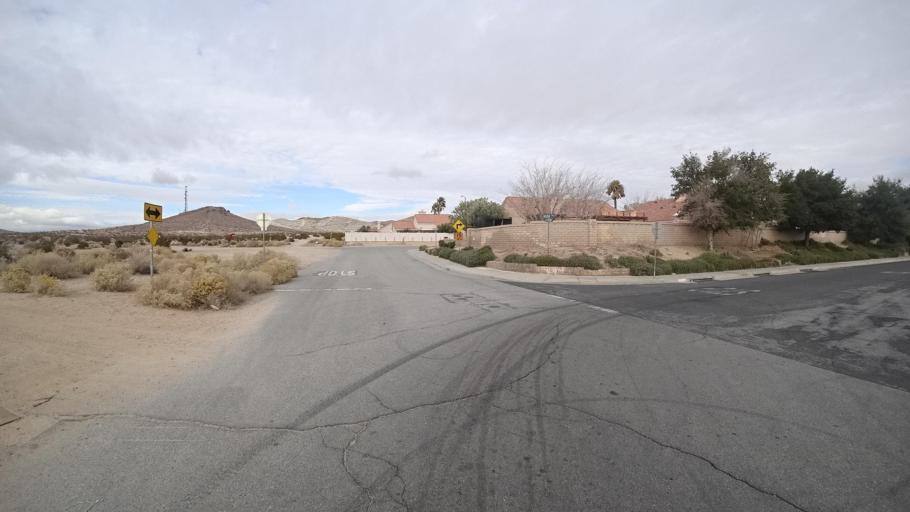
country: US
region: California
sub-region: Kern County
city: Rosamond
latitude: 34.8735
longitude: -118.1583
